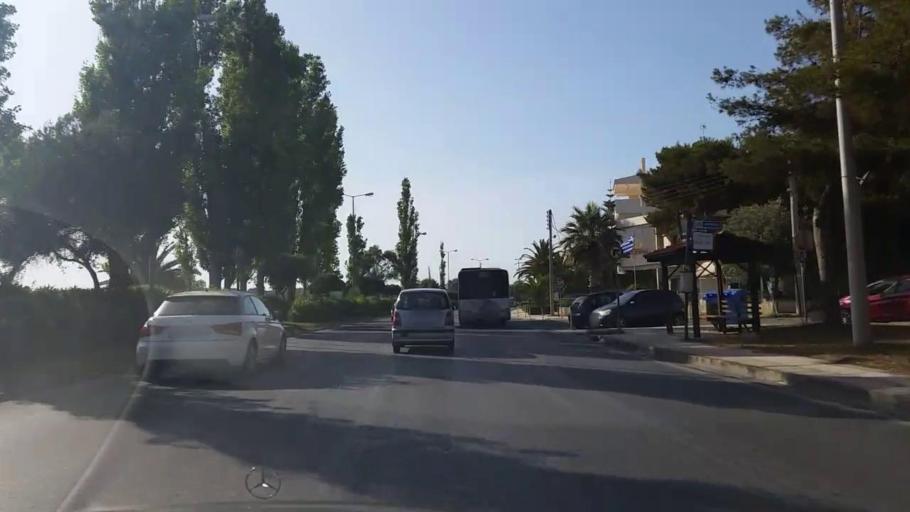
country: GR
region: Attica
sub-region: Nomarchia Athinas
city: Glyfada
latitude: 37.8456
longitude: 23.7549
